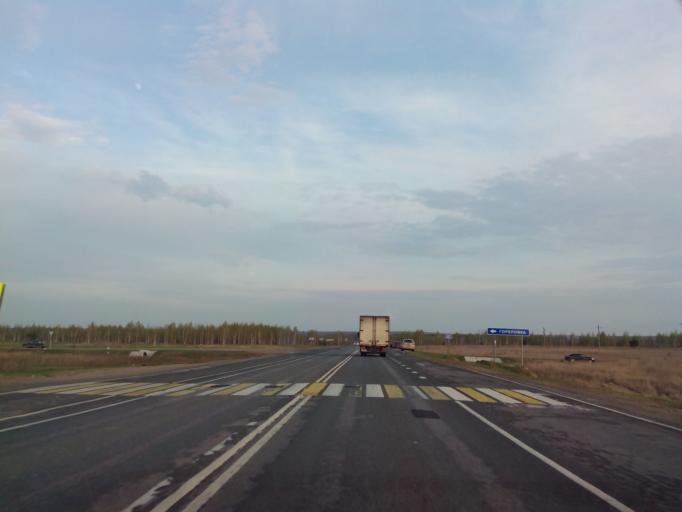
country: RU
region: Rjazan
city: Korablino
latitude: 53.7359
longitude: 39.8948
